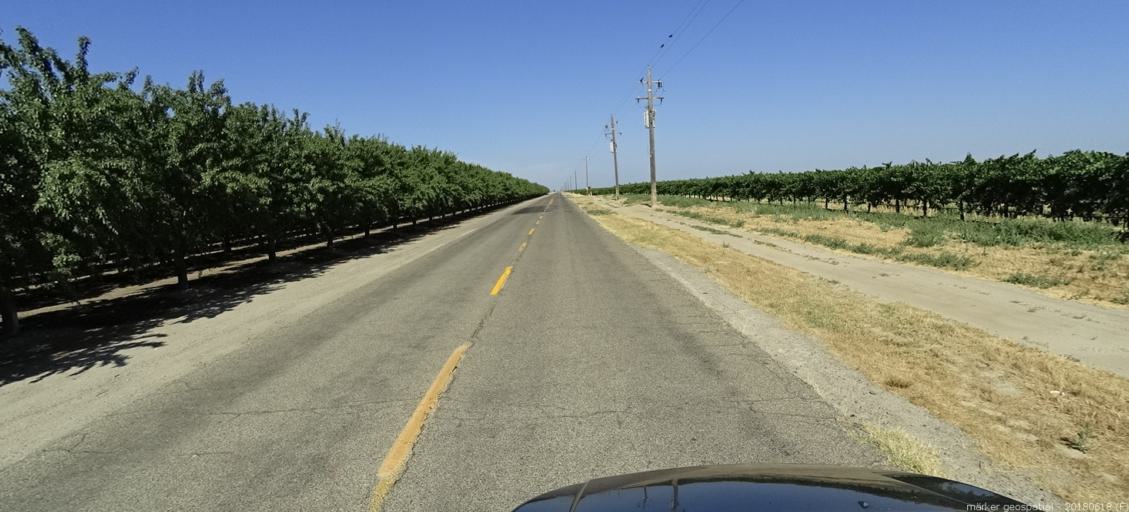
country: US
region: California
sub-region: Madera County
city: Parkwood
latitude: 36.8366
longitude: -120.1809
